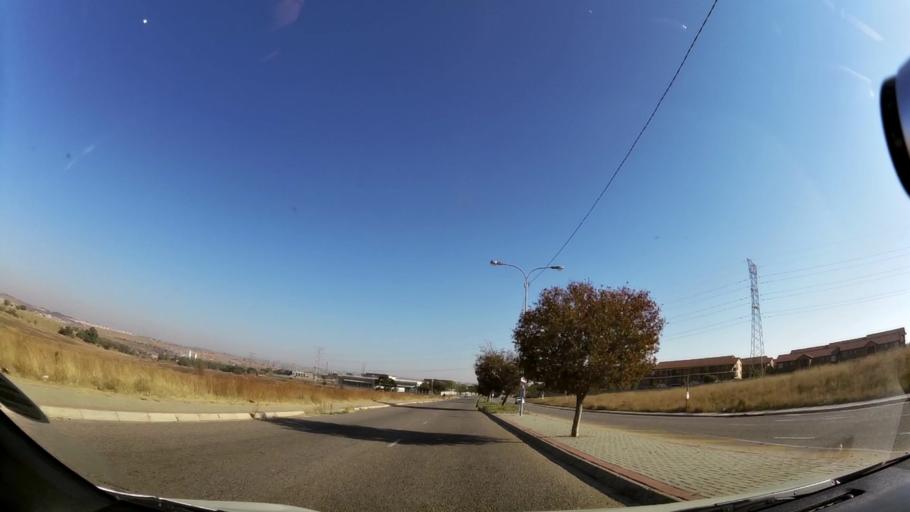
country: ZA
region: Gauteng
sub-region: City of Johannesburg Metropolitan Municipality
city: Midrand
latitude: -25.9218
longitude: 28.1315
